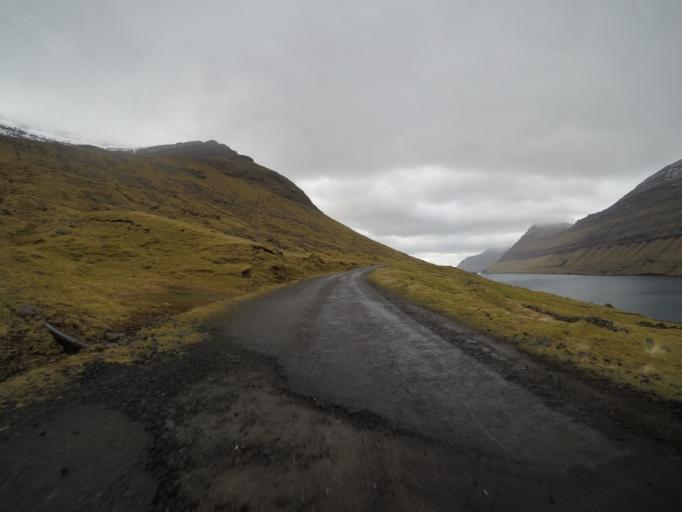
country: FO
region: Nordoyar
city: Klaksvik
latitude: 62.3022
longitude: -6.5369
